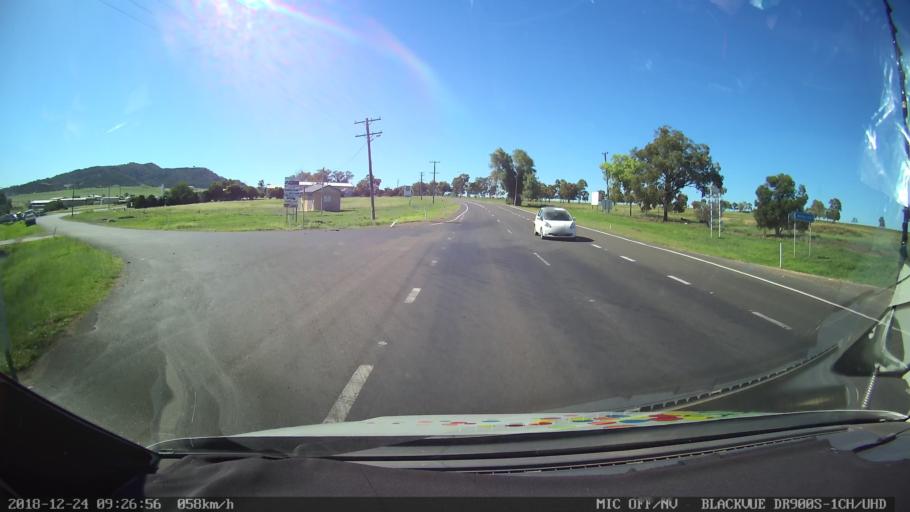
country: AU
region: New South Wales
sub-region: Liverpool Plains
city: Quirindi
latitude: -31.5237
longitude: 150.6786
